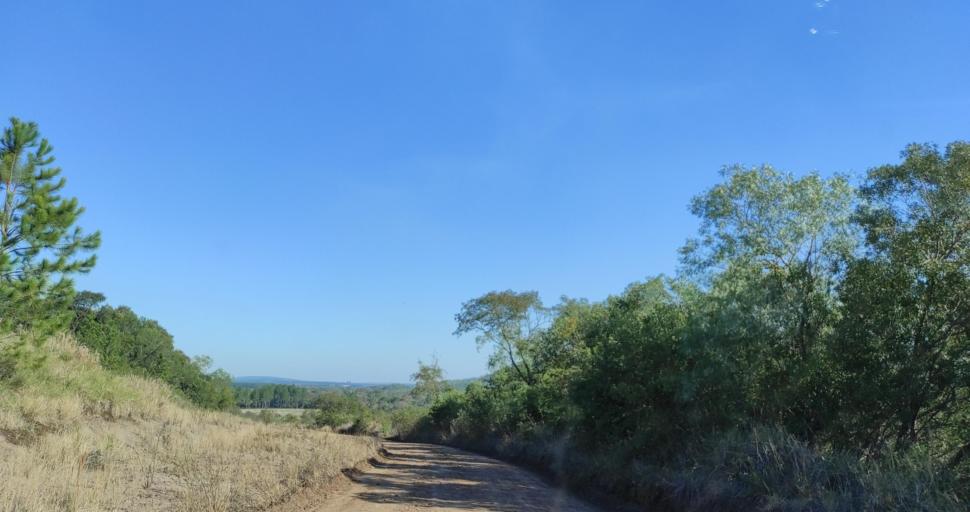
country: AR
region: Misiones
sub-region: Departamento de Apostoles
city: San Jose
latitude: -27.6698
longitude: -55.6612
